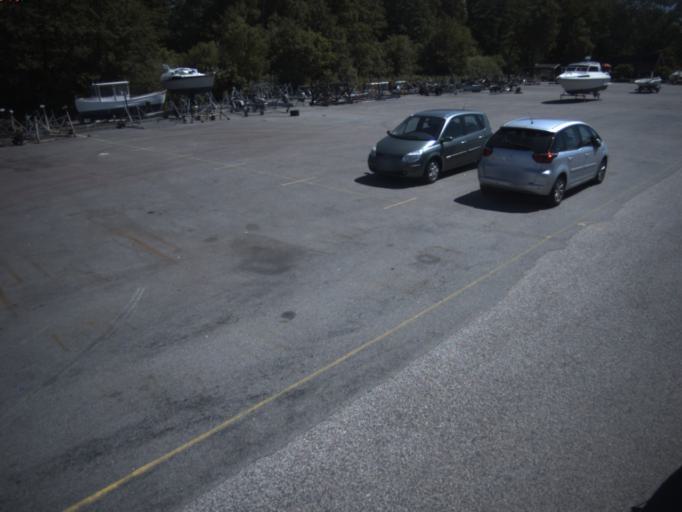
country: SE
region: Skane
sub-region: Helsingborg
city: Rydeback
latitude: 55.9916
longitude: 12.7473
